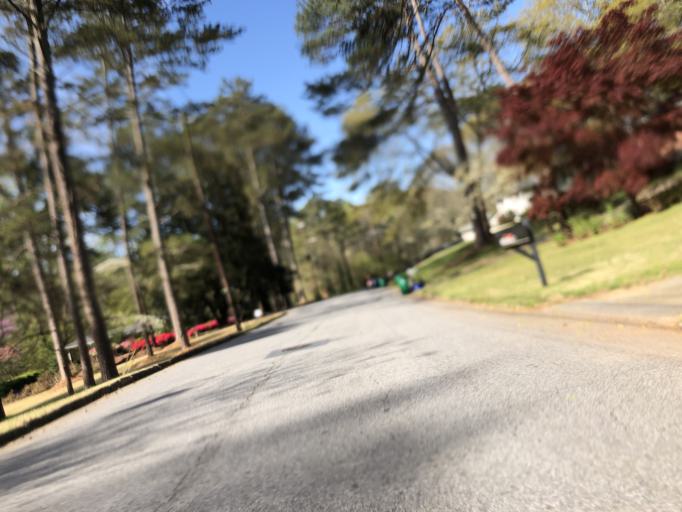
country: US
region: Georgia
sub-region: DeKalb County
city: North Decatur
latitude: 33.8067
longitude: -84.2960
